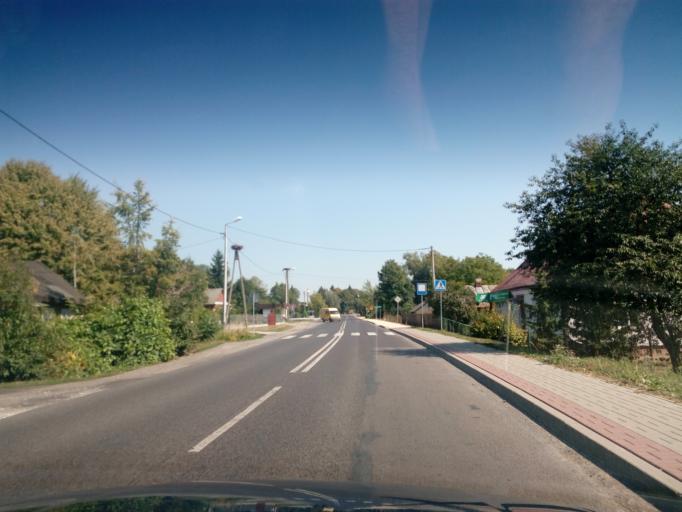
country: PL
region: Lublin Voivodeship
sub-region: Powiat hrubieszowski
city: Horodlo
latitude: 50.8425
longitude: 24.0211
